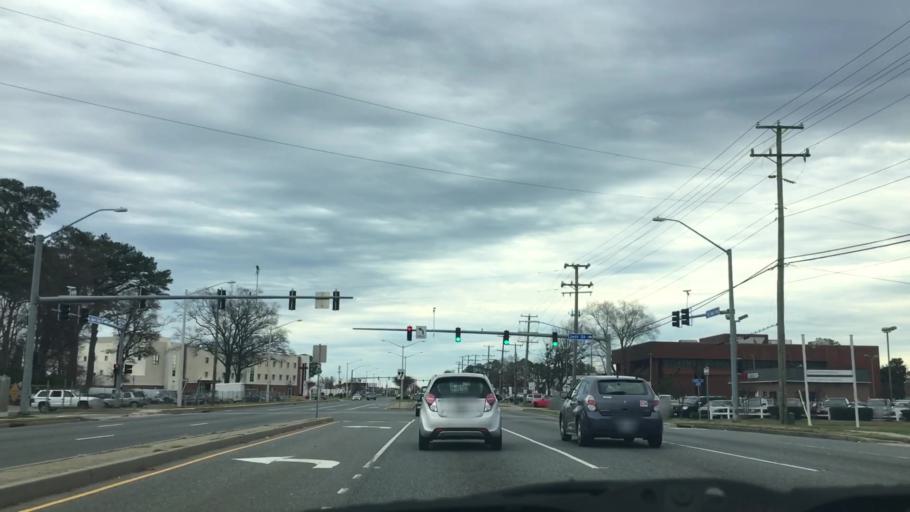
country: US
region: Virginia
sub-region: City of Norfolk
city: Norfolk
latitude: 36.8564
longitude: -76.2264
